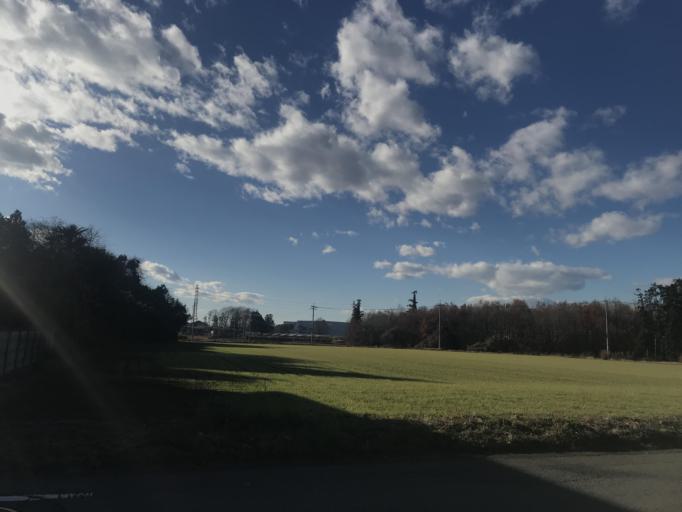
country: JP
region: Tochigi
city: Kaminokawa
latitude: 36.4179
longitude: 139.8773
